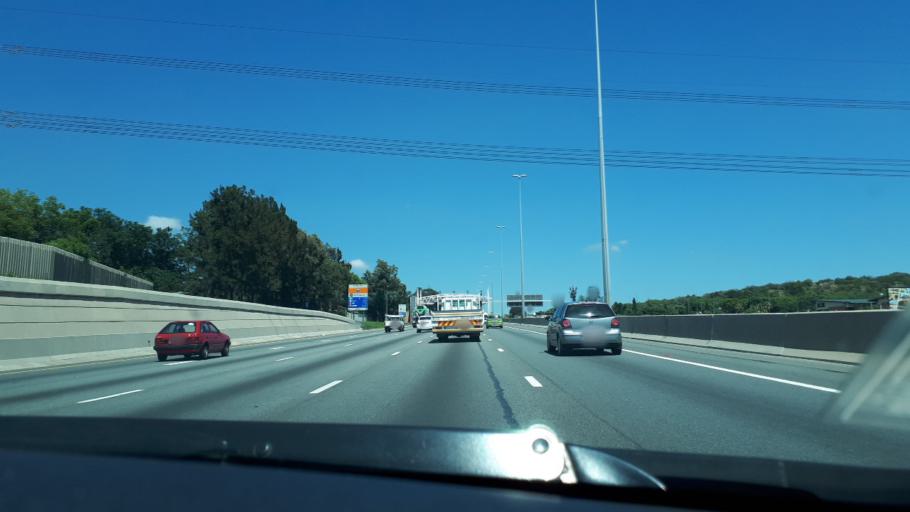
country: ZA
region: Gauteng
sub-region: City of Johannesburg Metropolitan Municipality
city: Midrand
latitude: -26.0369
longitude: 28.0464
